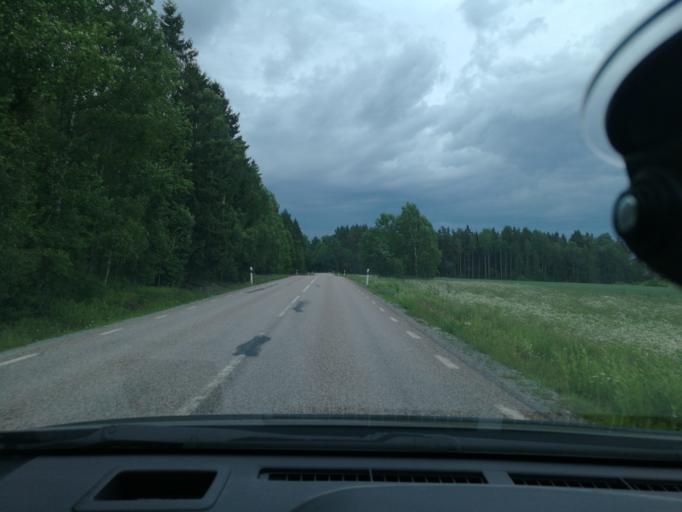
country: SE
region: Vaestmanland
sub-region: Sala Kommun
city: Sala
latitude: 59.9159
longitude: 16.4811
